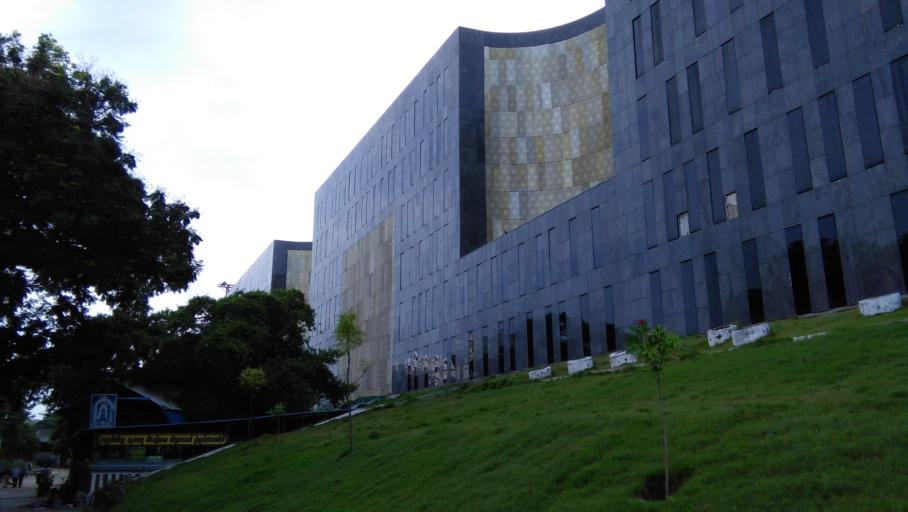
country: IN
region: Tamil Nadu
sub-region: Chennai
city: Chennai
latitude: 13.0698
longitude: 80.2748
